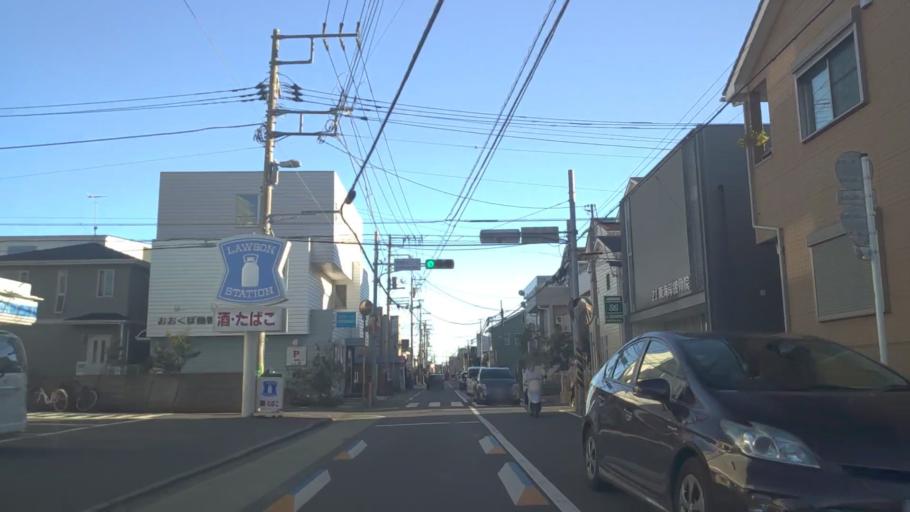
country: JP
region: Kanagawa
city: Chigasaki
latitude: 35.3277
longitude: 139.4146
